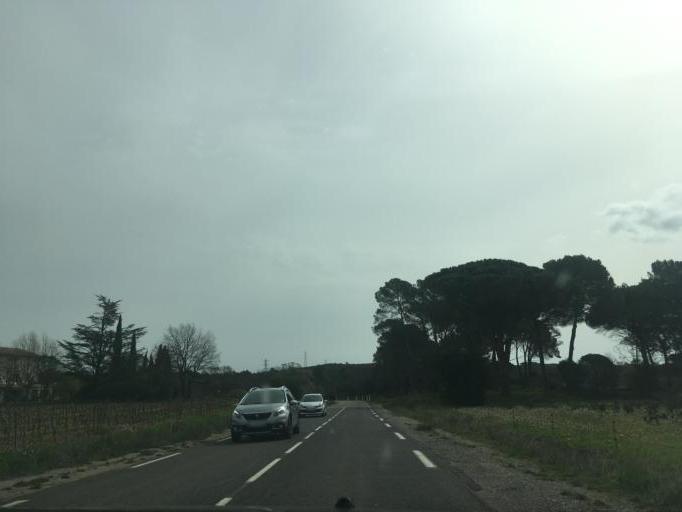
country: FR
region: Provence-Alpes-Cote d'Azur
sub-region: Departement du Var
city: Le Muy
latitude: 43.4929
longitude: 6.5685
